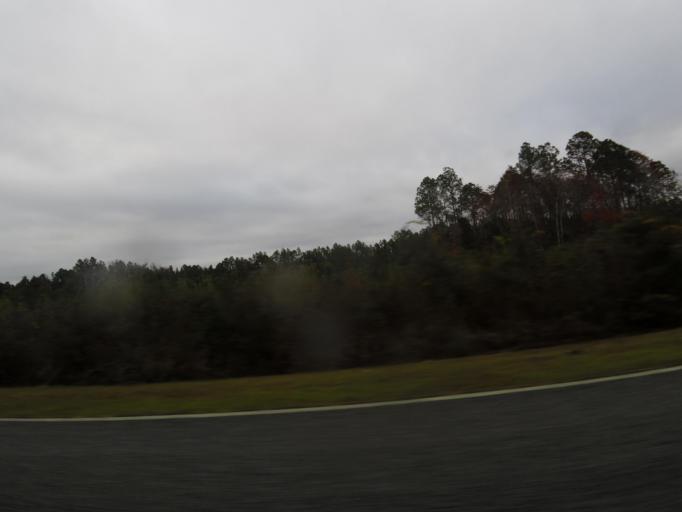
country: US
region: Georgia
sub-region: Charlton County
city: Folkston
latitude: 30.8913
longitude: -82.0633
